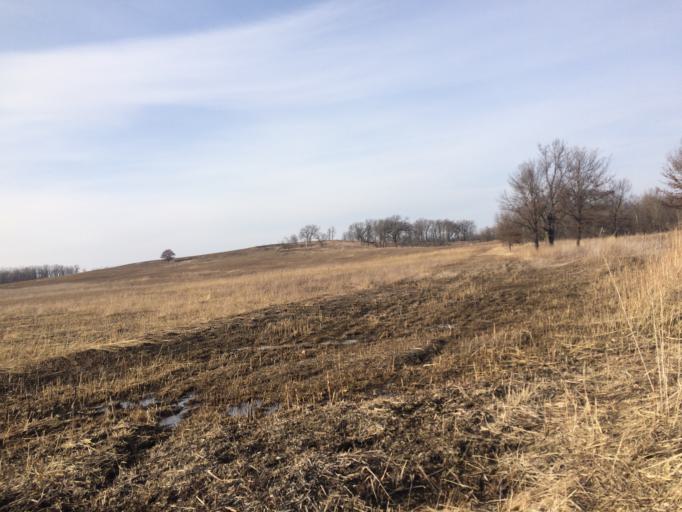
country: US
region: Illinois
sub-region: Cook County
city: Streamwood
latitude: 42.0562
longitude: -88.1984
